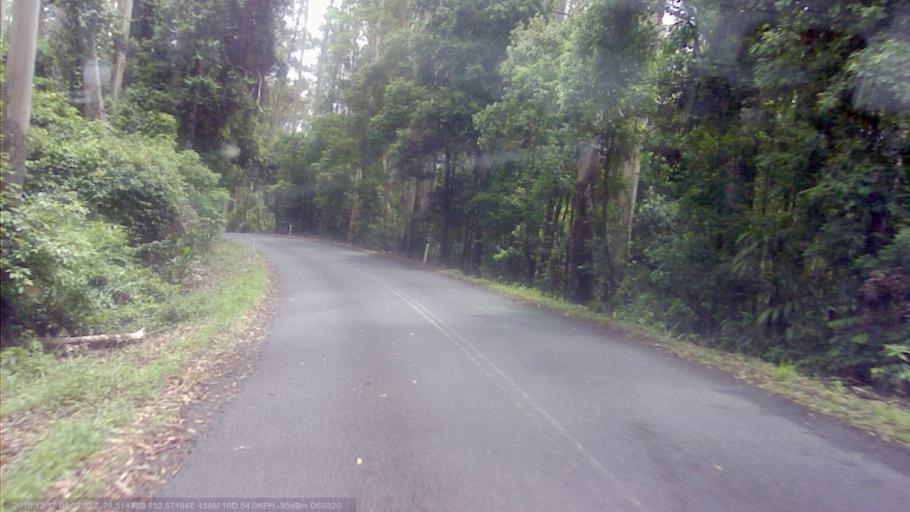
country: AU
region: New South Wales
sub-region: Kyogle
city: Kyogle
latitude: -28.5143
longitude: 152.5718
